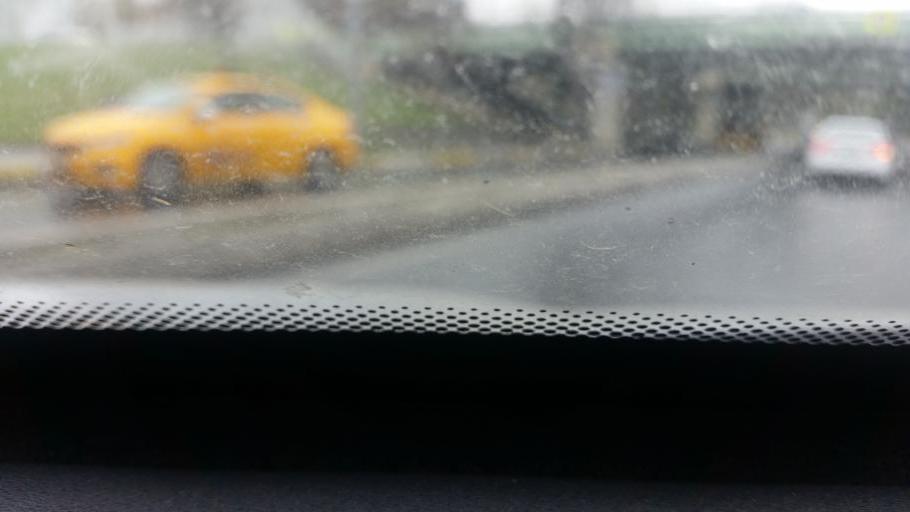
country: TR
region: Istanbul
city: Bahcelievler
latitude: 40.9752
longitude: 28.8662
